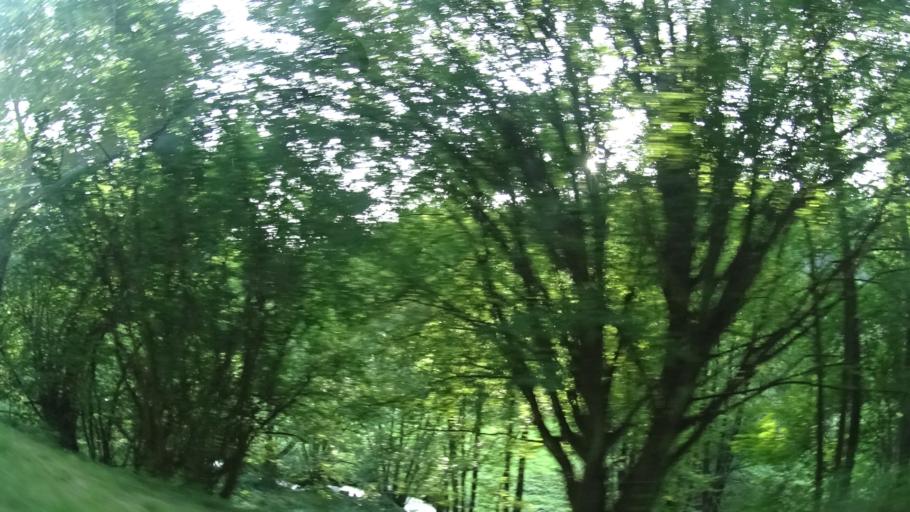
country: DE
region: Hesse
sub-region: Regierungsbezirk Darmstadt
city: Rothenberg
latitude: 49.5385
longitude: 8.9218
